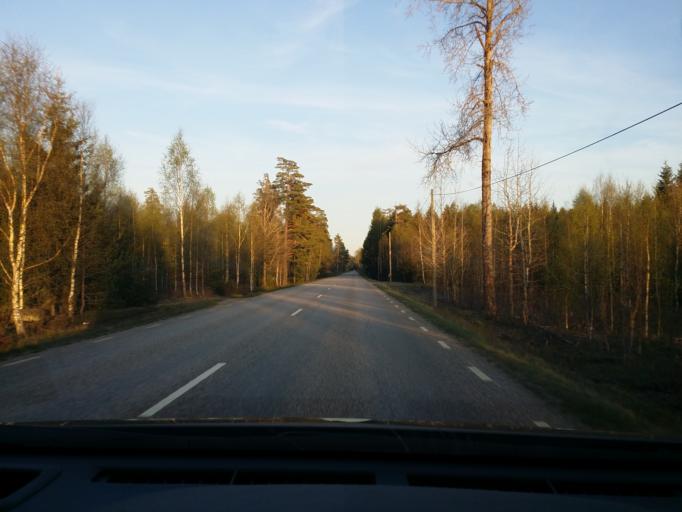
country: SE
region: Vaestmanland
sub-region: Sala Kommun
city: Sala
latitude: 59.8314
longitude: 16.5107
